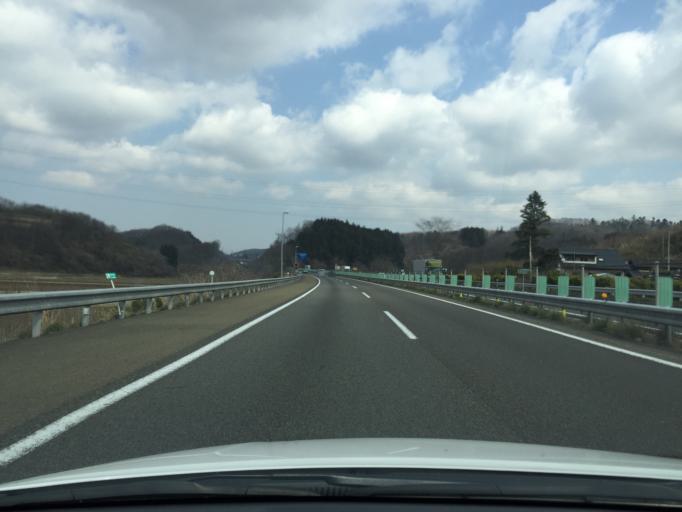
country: JP
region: Miyagi
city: Iwanuma
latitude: 38.1738
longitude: 140.7700
